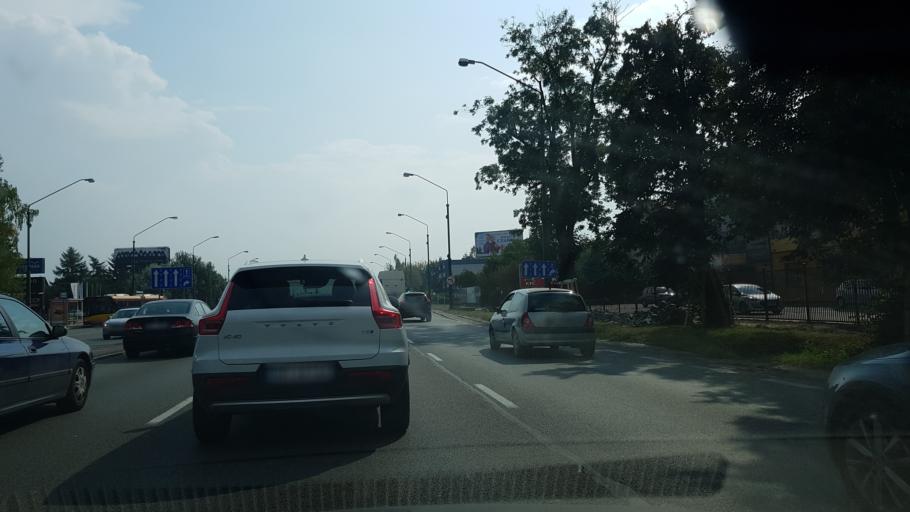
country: PL
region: Masovian Voivodeship
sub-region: Powiat piaseczynski
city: Mysiadlo
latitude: 52.1189
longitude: 21.0182
